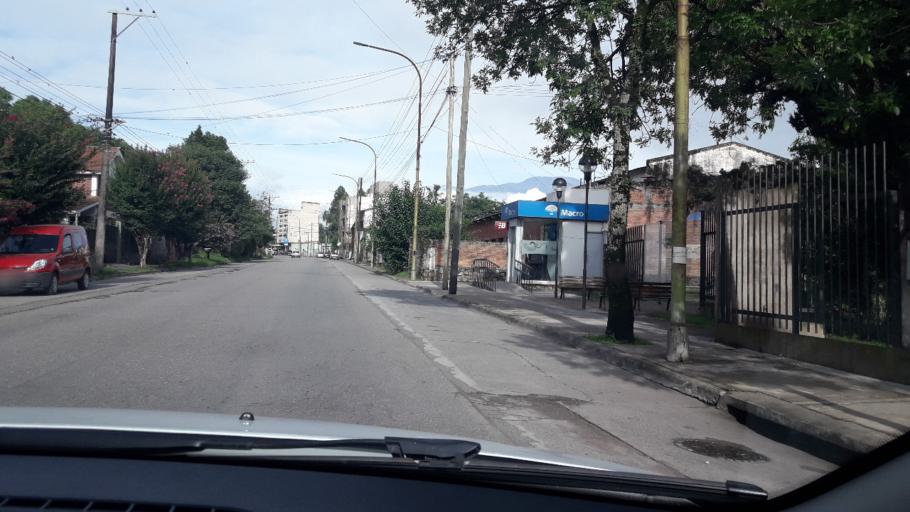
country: AR
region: Jujuy
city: San Salvador de Jujuy
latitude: -24.1789
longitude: -65.3297
